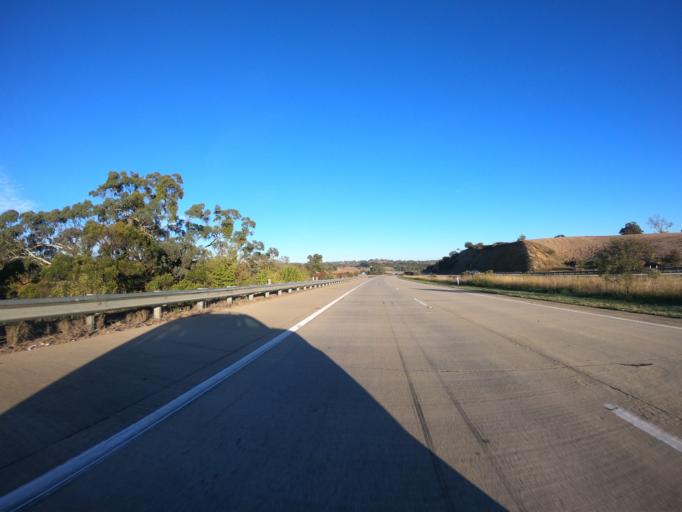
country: AU
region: New South Wales
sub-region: Yass Valley
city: Gundaroo
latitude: -35.1766
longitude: 149.2859
